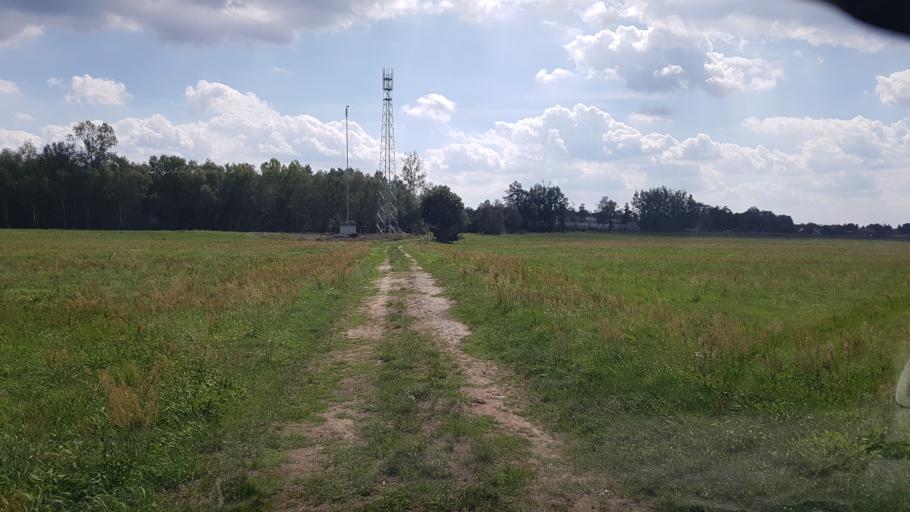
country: DE
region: Brandenburg
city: Lubbenau
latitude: 51.8245
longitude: 13.9102
